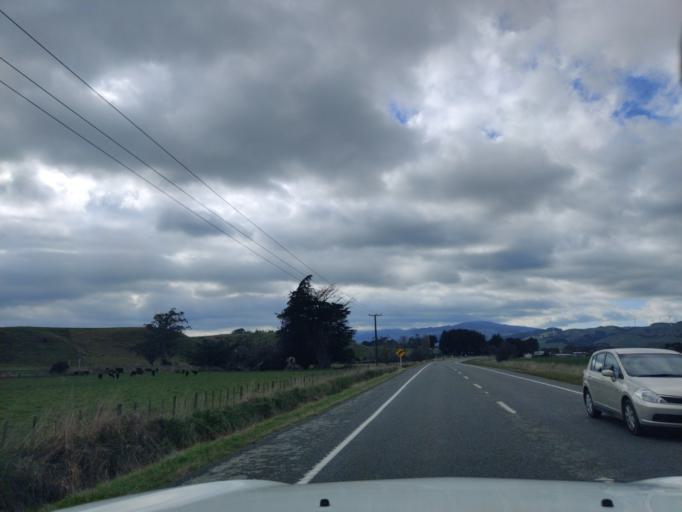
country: NZ
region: Manawatu-Wanganui
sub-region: Palmerston North City
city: Palmerston North
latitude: -40.3022
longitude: 175.7330
